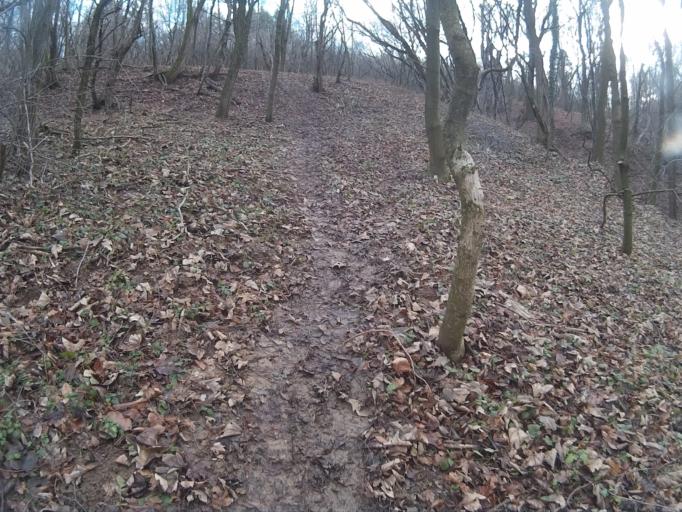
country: HU
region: Veszprem
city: Urkut
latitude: 47.1391
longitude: 17.6490
